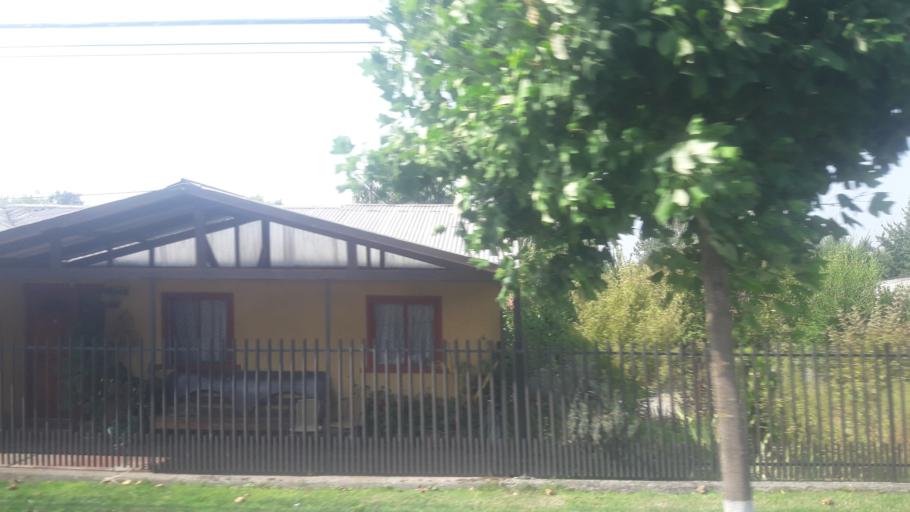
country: CL
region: Biobio
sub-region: Provincia de Concepcion
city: Lota
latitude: -37.1706
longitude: -72.9455
